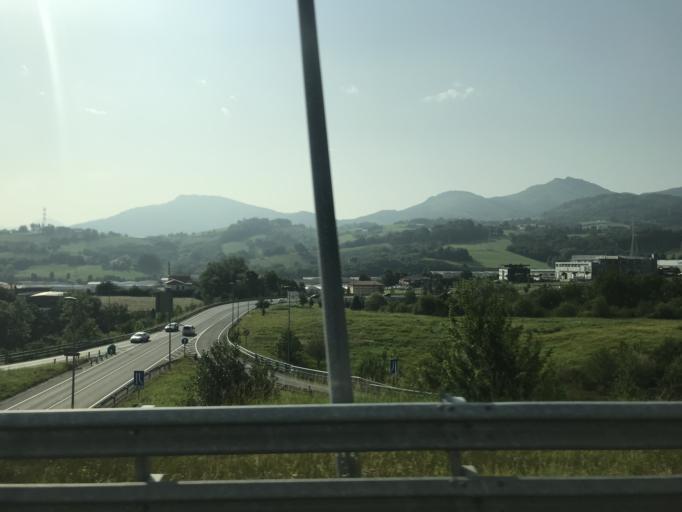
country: ES
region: Basque Country
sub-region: Provincia de Guipuzcoa
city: Urnieta
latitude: 43.2429
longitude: -1.9992
